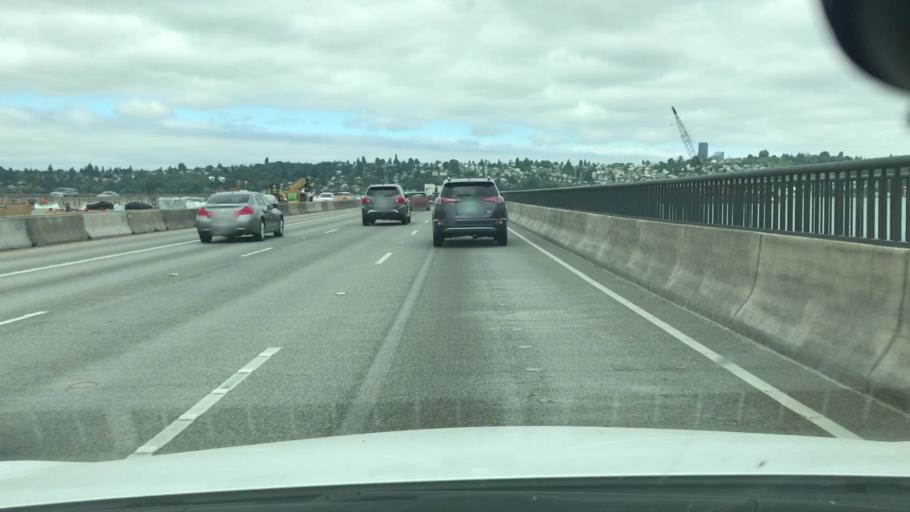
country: US
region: Washington
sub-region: King County
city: Mercer Island
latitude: 47.5902
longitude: -122.2634
